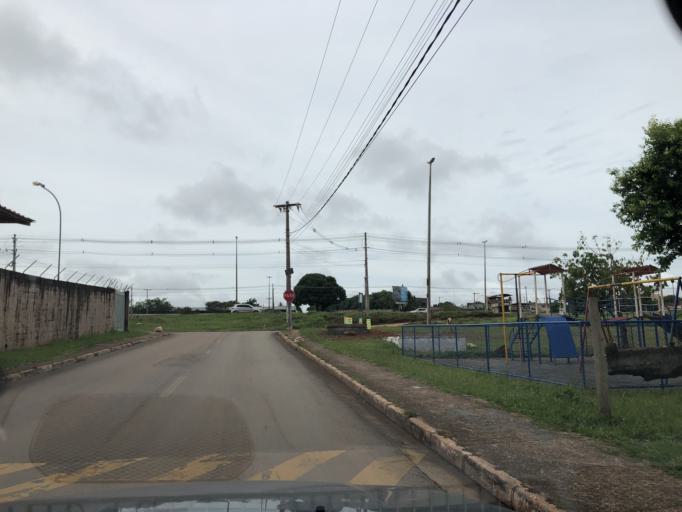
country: BR
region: Federal District
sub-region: Brasilia
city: Brasilia
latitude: -15.7856
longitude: -48.1387
